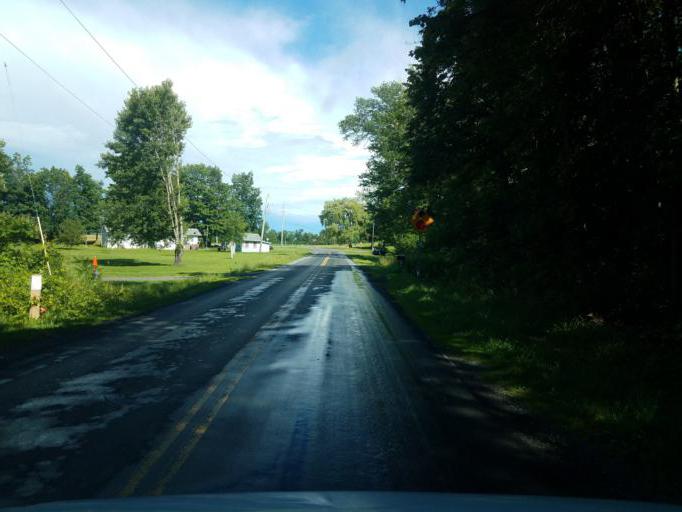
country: US
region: New York
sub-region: Wayne County
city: Clyde
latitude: 43.0081
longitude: -76.8584
